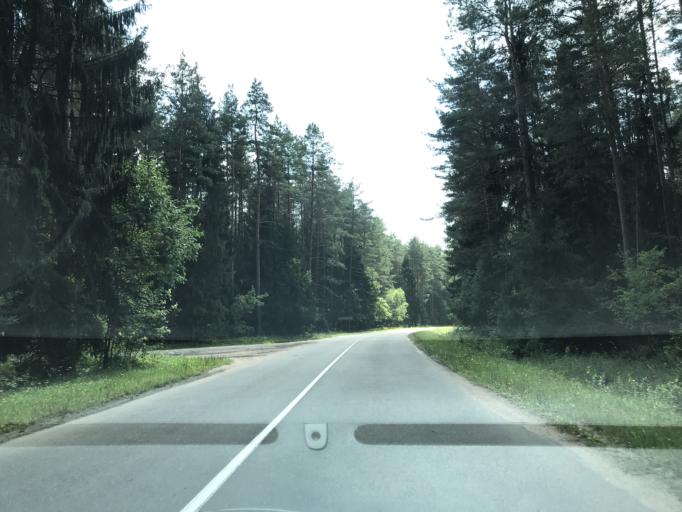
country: BY
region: Minsk
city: Rakaw
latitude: 53.9927
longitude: 26.9910
